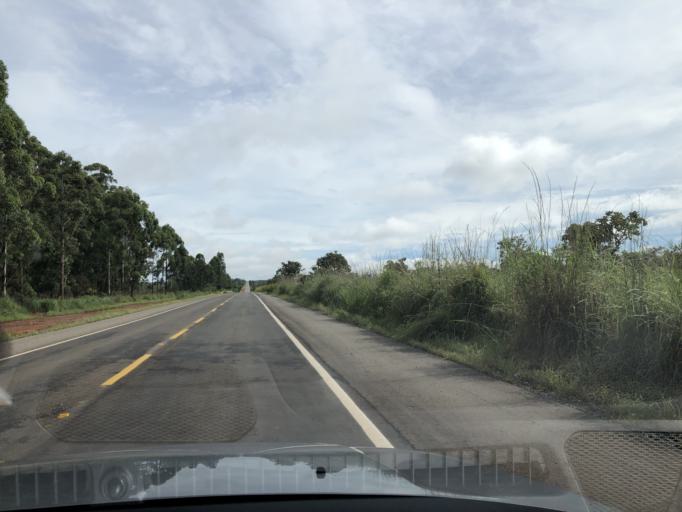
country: BR
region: Federal District
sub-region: Brasilia
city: Brasilia
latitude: -15.6739
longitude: -48.0887
